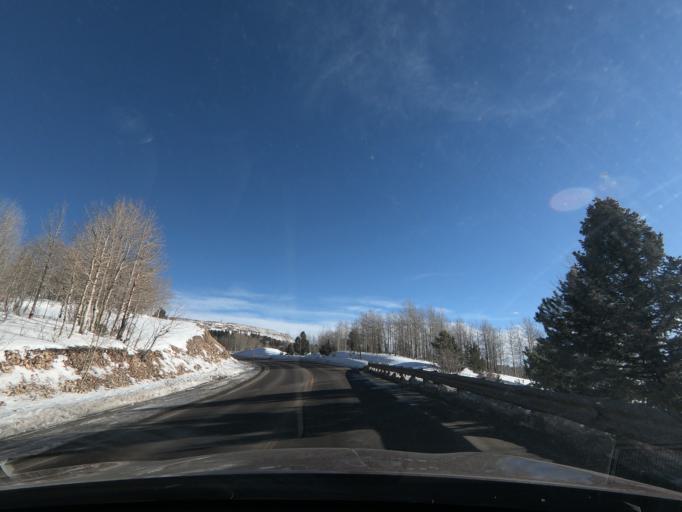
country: US
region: Colorado
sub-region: Teller County
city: Cripple Creek
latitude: 38.7517
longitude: -105.1652
